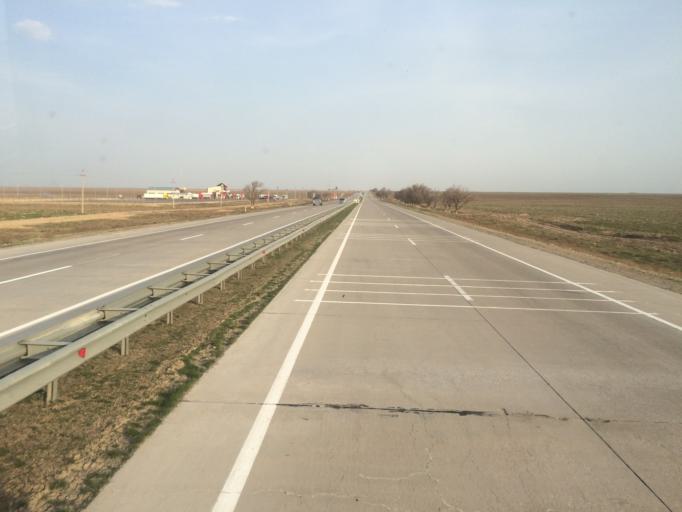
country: KZ
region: Ongtustik Qazaqstan
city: Temirlanovka
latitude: 42.8427
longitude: 69.1009
